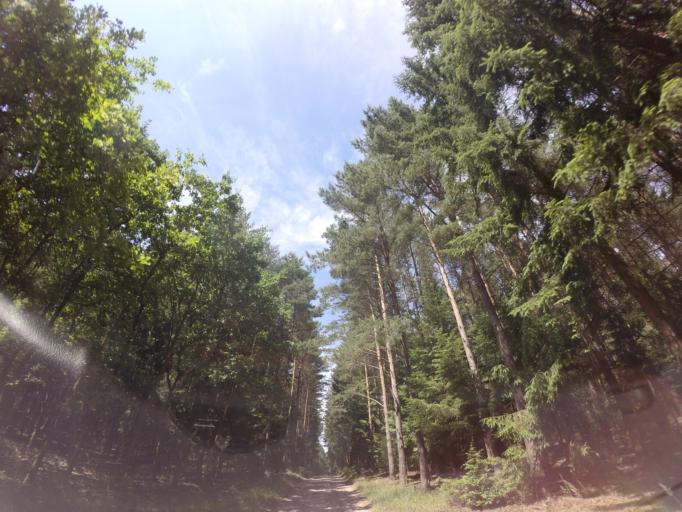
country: PL
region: West Pomeranian Voivodeship
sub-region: Powiat choszczenski
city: Recz
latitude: 53.3305
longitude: 15.5251
